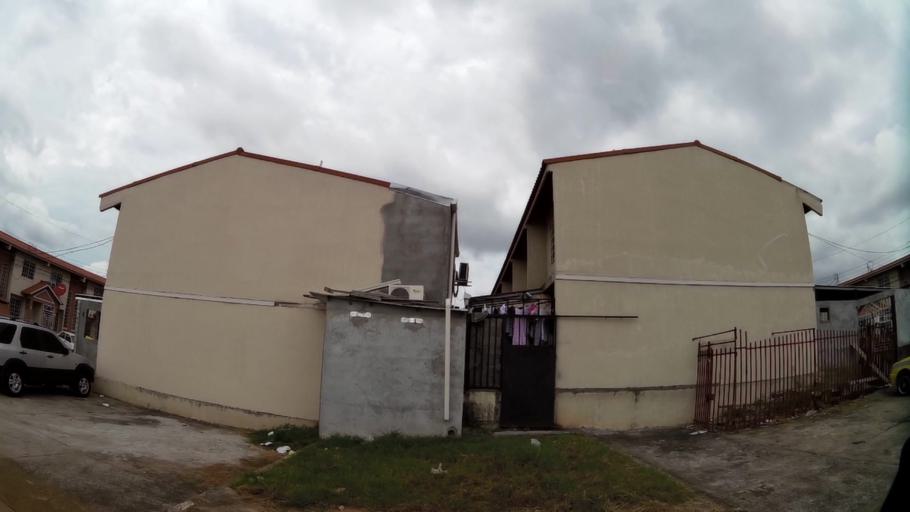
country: PA
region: Panama
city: San Miguelito
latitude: 9.0602
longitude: -79.4246
